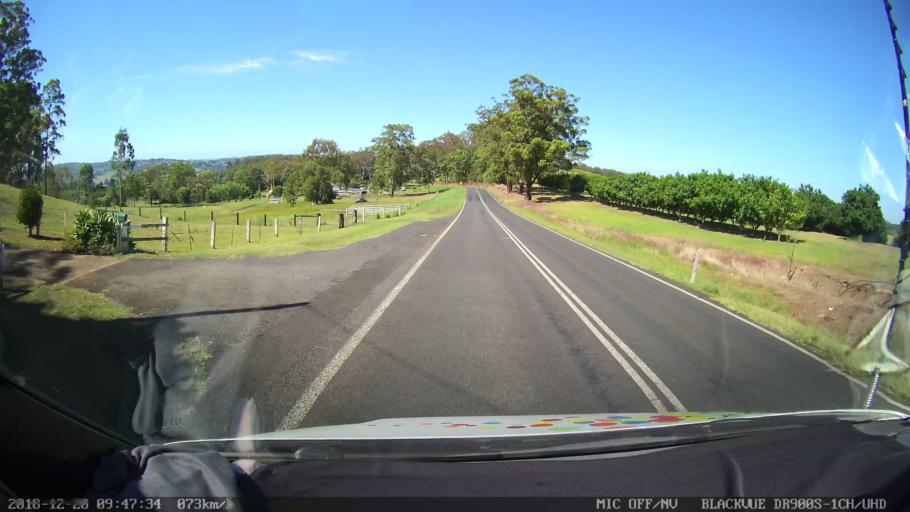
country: AU
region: New South Wales
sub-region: Lismore Municipality
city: Lismore
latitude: -28.7643
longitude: 153.2962
